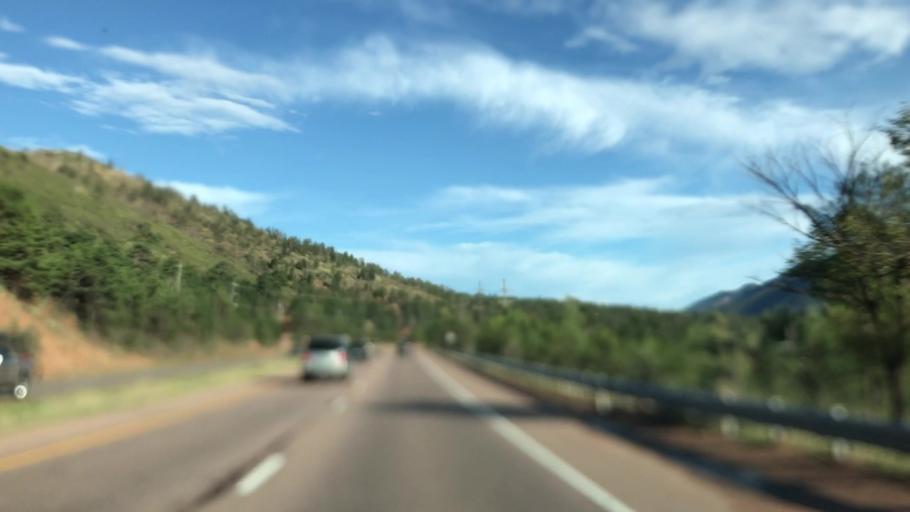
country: US
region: Colorado
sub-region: El Paso County
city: Cascade-Chipita Park
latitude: 38.9097
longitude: -104.9742
